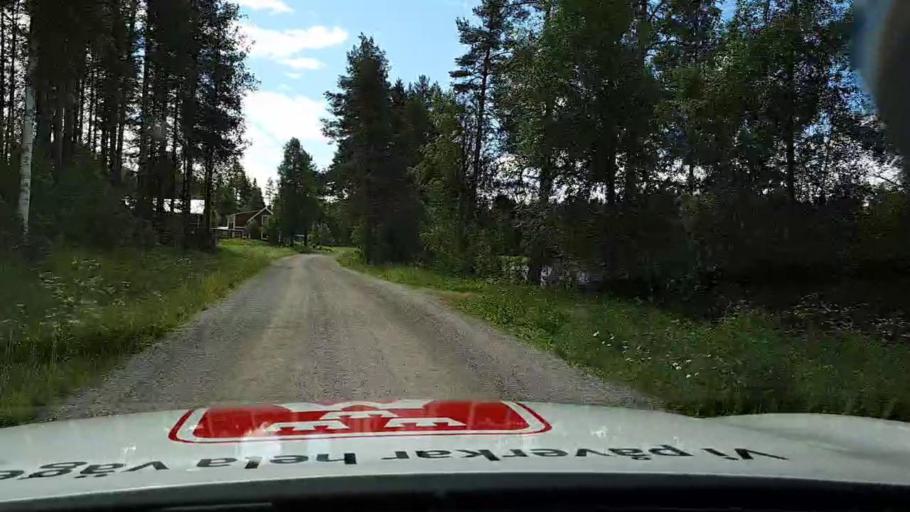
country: SE
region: Jaemtland
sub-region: Braecke Kommun
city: Braecke
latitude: 62.7505
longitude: 15.5024
